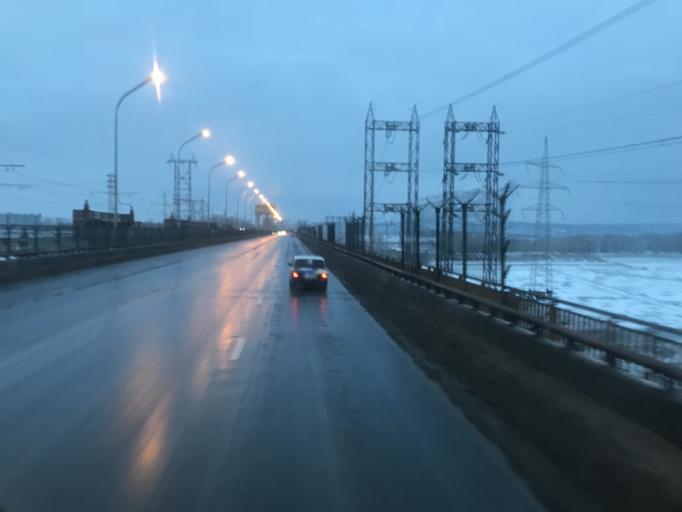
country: RU
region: Samara
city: Zhigulevsk
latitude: 53.4568
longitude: 49.4953
